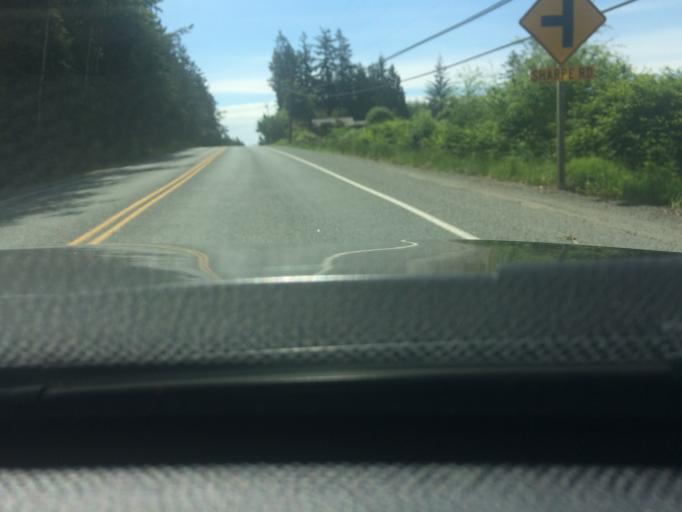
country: US
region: Washington
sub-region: Skagit County
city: Anacortes
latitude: 48.4352
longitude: -122.6645
